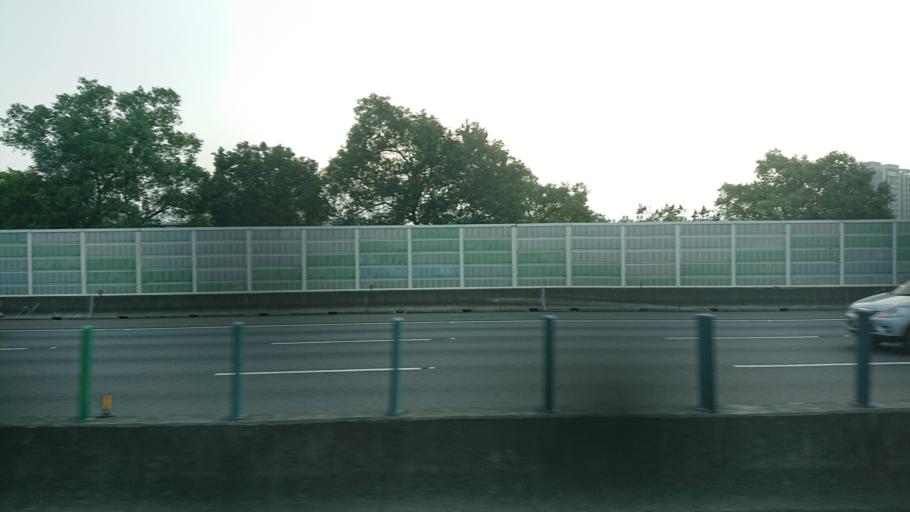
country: TW
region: Taiwan
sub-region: Changhua
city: Chang-hua
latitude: 24.1147
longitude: 120.5948
